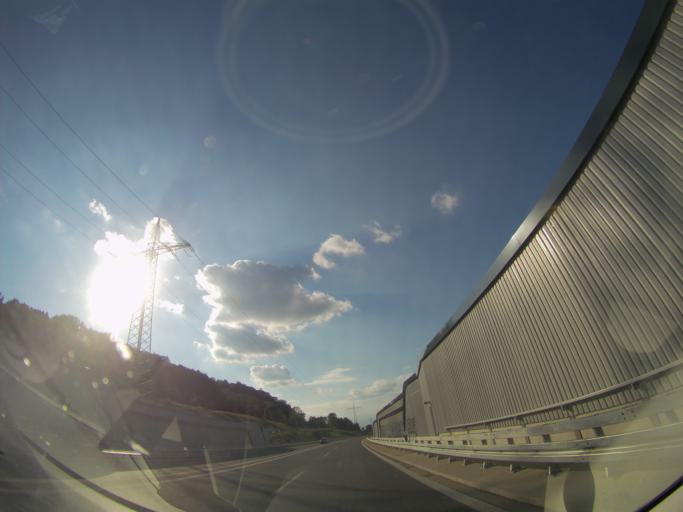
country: DE
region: Baden-Wuerttemberg
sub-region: Regierungsbezirk Stuttgart
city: Gingen an der Fils
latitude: 48.6538
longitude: 9.7785
